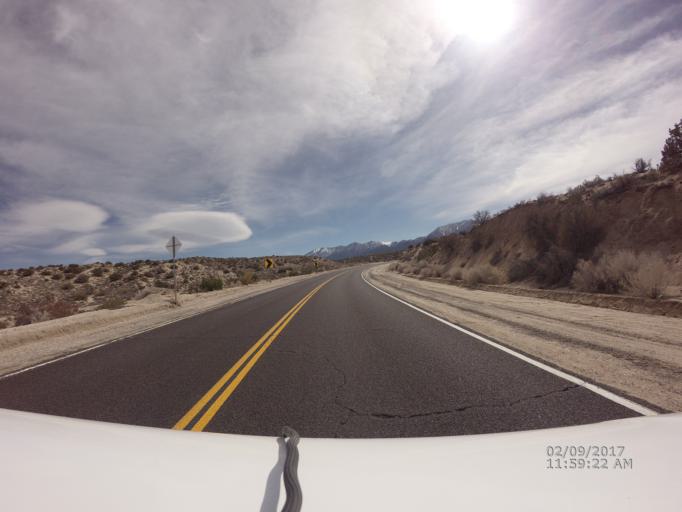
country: US
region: California
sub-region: Los Angeles County
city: Littlerock
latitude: 34.4749
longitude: -117.9010
